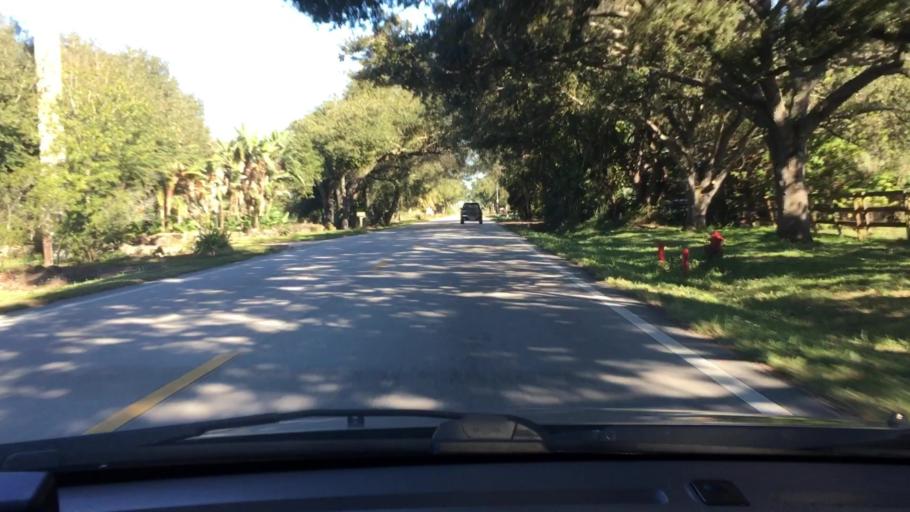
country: US
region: Florida
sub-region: Indian River County
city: Winter Beach
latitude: 27.7363
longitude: -80.4621
